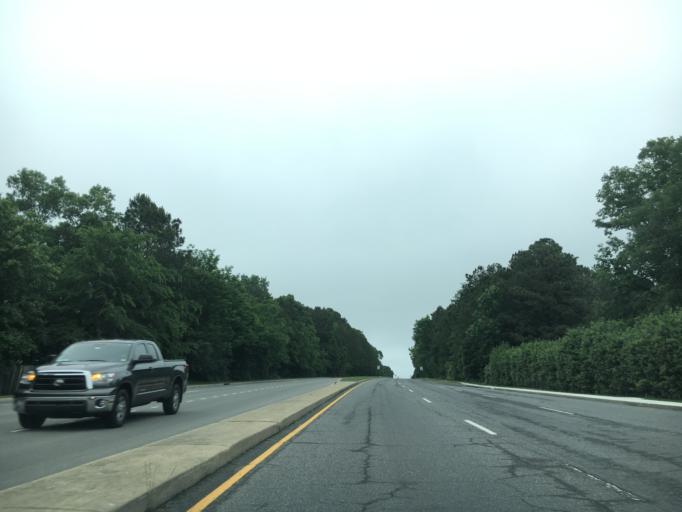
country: US
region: Virginia
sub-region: Henrico County
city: Short Pump
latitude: 37.6134
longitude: -77.6314
